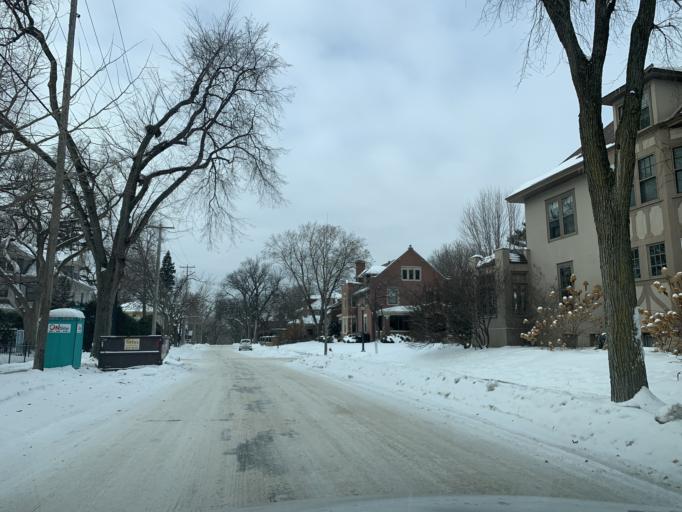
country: US
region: Minnesota
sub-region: Hennepin County
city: Minneapolis
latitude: 44.9655
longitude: -93.3002
